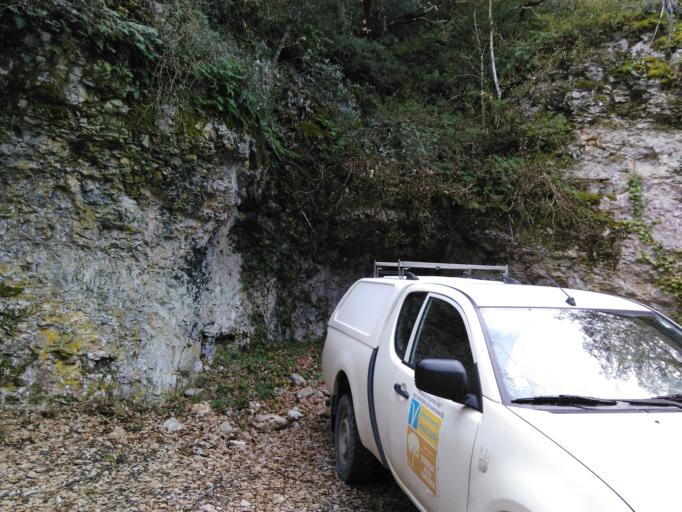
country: FR
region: Provence-Alpes-Cote d'Azur
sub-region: Departement du Vaucluse
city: Villes-sur-Auzon
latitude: 44.1044
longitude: 5.2474
